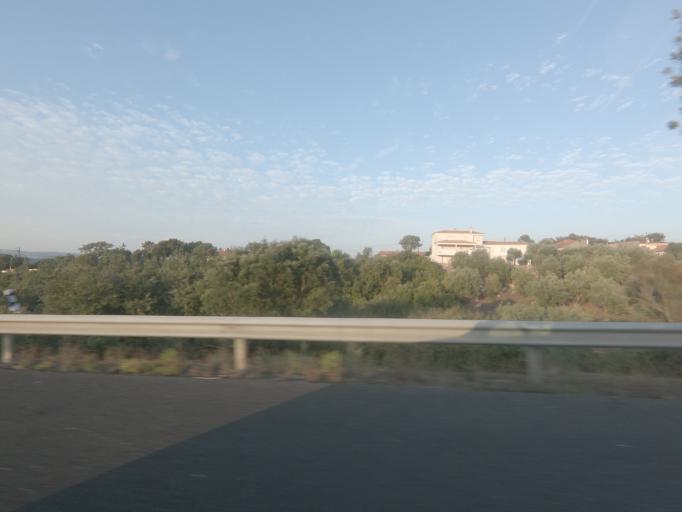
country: PT
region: Leiria
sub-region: Leiria
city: Santa Catarina da Serra
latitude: 39.6979
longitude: -8.6956
